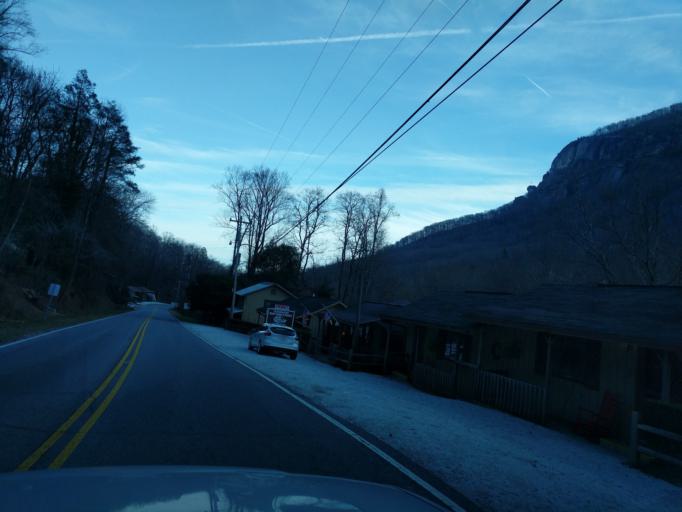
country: US
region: North Carolina
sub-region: Rutherford County
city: Lake Lure
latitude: 35.4421
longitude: -82.2591
